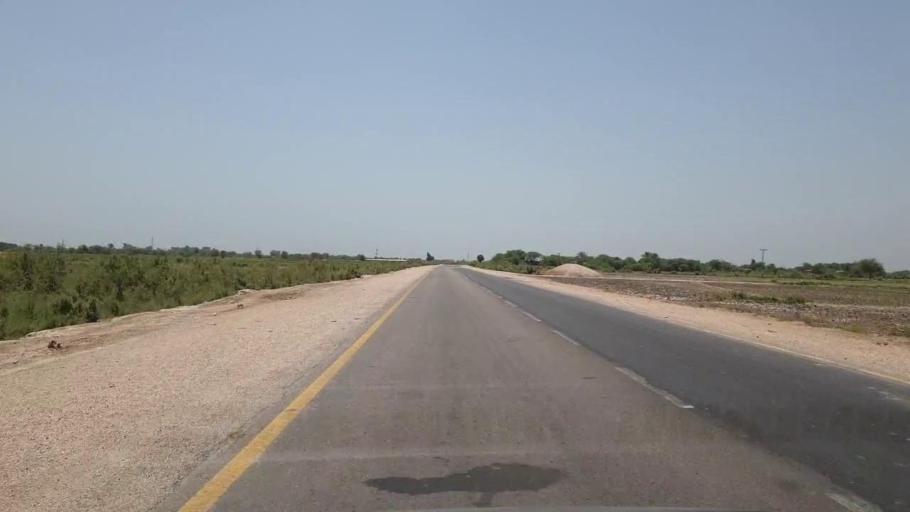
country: PK
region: Sindh
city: Sakrand
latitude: 26.1256
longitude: 68.3808
